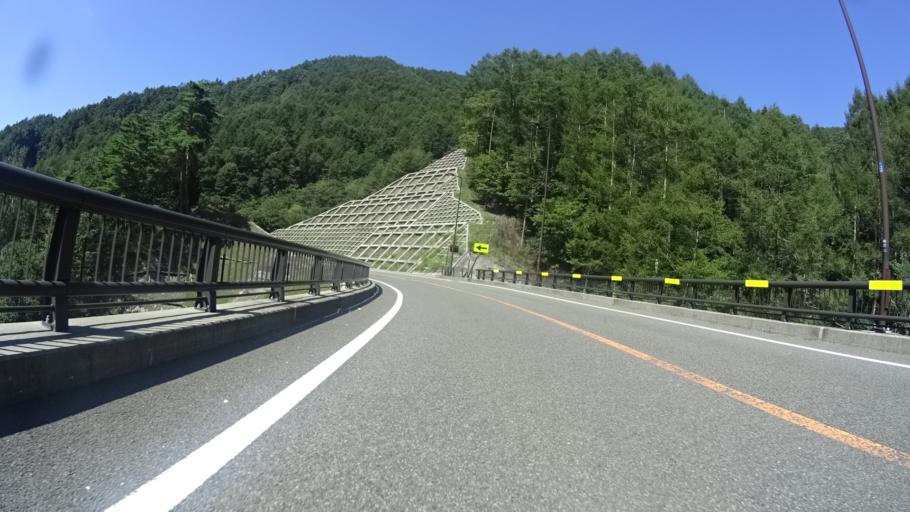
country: JP
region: Yamanashi
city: Enzan
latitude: 35.7658
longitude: 138.8047
